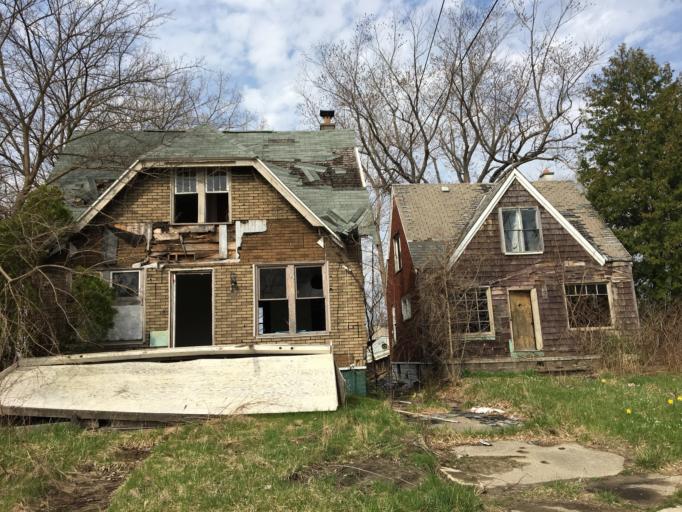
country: US
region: Michigan
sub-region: Oakland County
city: Hazel Park
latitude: 42.4441
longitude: -83.1096
